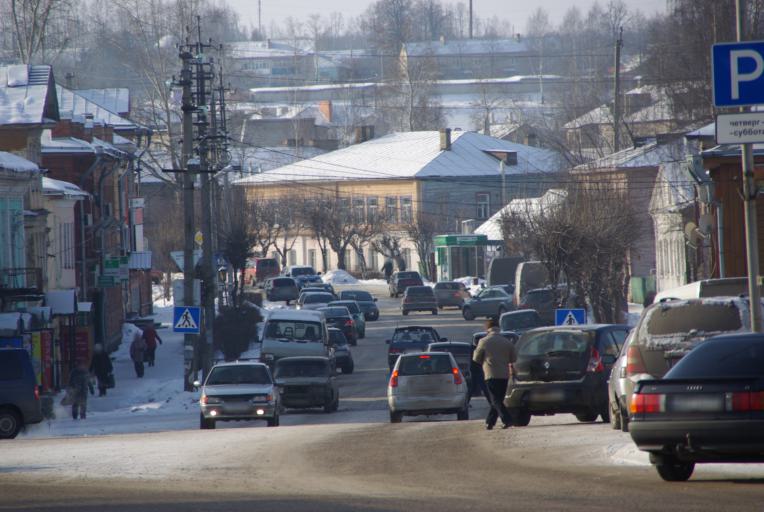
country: RU
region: Kostroma
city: Galich
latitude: 58.3810
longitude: 42.3476
